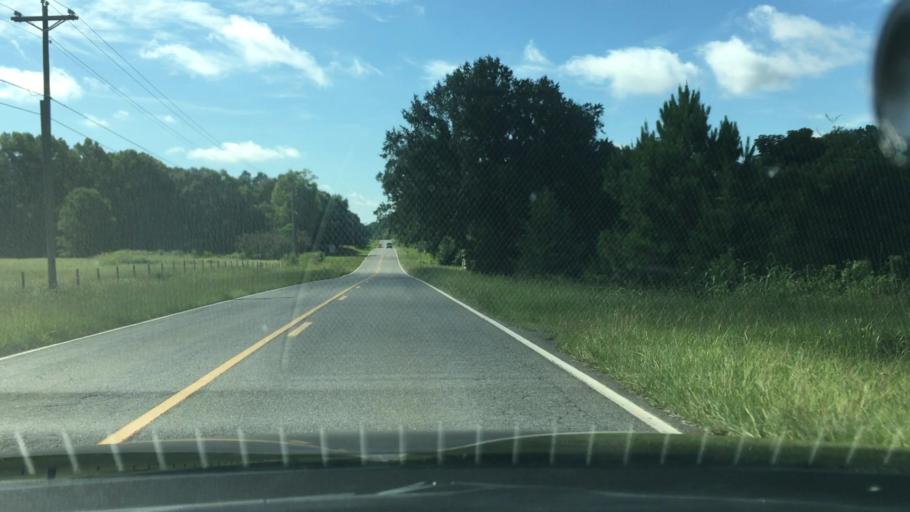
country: US
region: Georgia
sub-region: Putnam County
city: Jefferson
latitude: 33.4501
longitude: -83.2977
